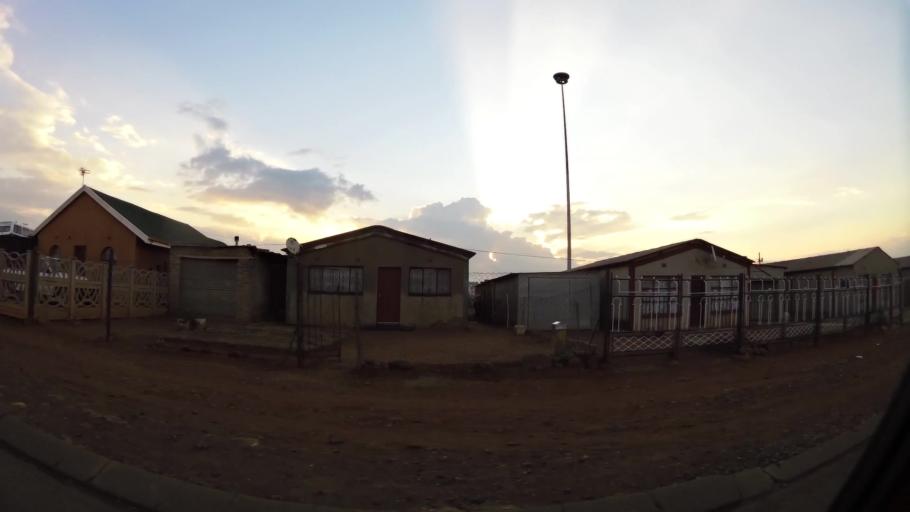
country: ZA
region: Gauteng
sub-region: City of Johannesburg Metropolitan Municipality
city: Orange Farm
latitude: -26.5563
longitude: 27.8624
